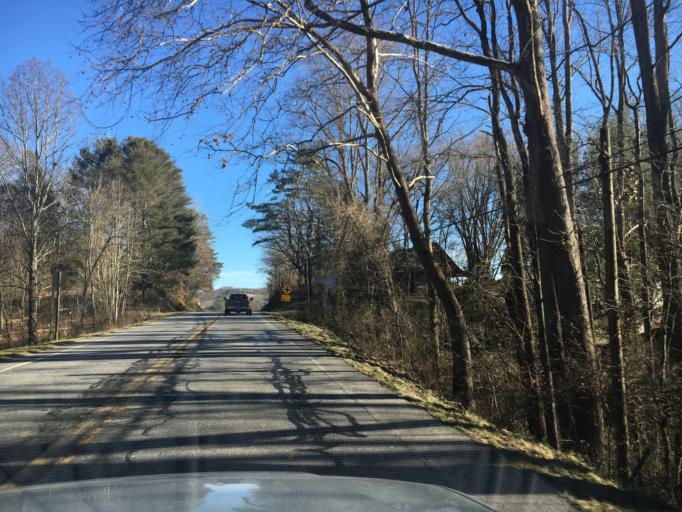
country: US
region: Georgia
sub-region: Union County
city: Blairsville
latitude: 34.8498
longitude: -83.9421
